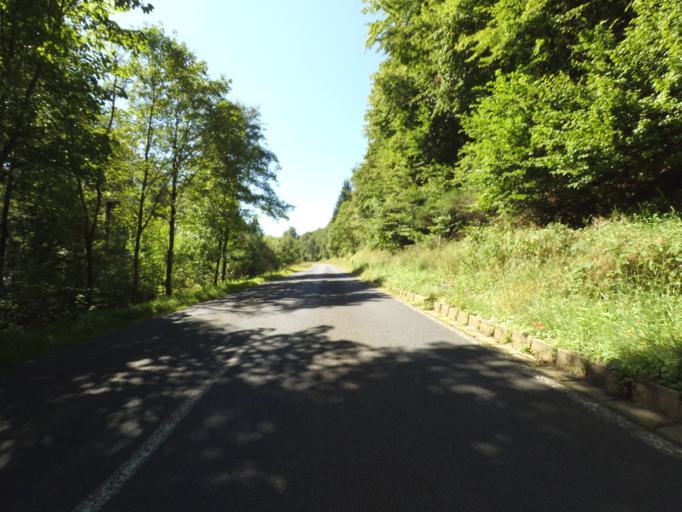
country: DE
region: Rheinland-Pfalz
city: Schutz
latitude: 50.1302
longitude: 6.7368
